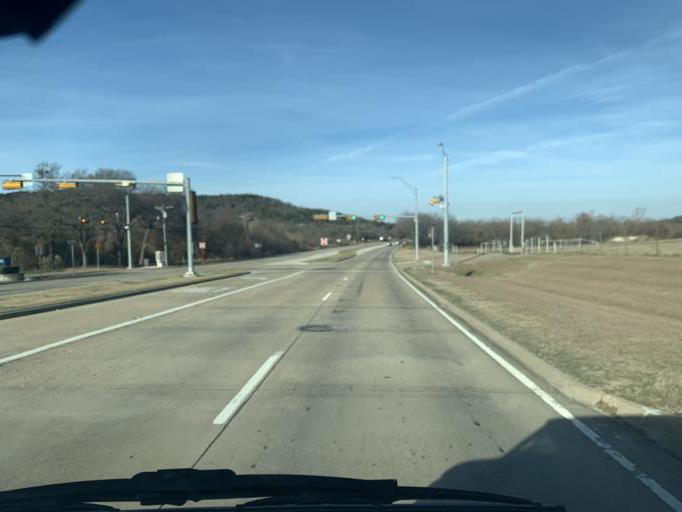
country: US
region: Texas
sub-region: Dallas County
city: Cedar Hill
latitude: 32.6133
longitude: -96.9668
